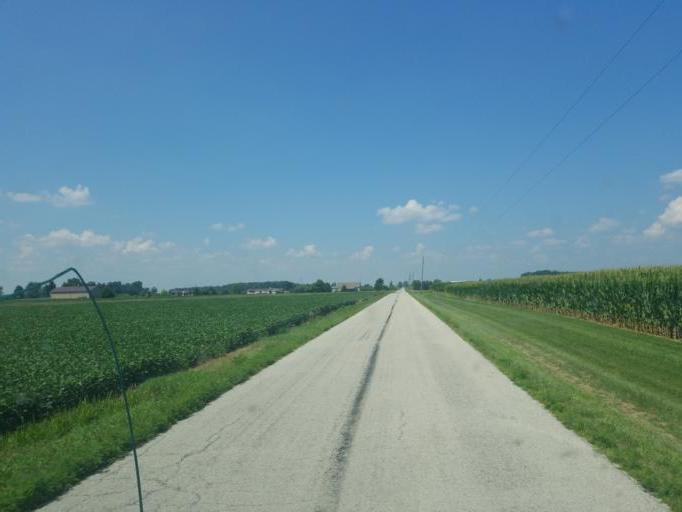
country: US
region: Ohio
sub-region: Shelby County
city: Jackson Center
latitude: 40.4069
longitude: -84.0691
